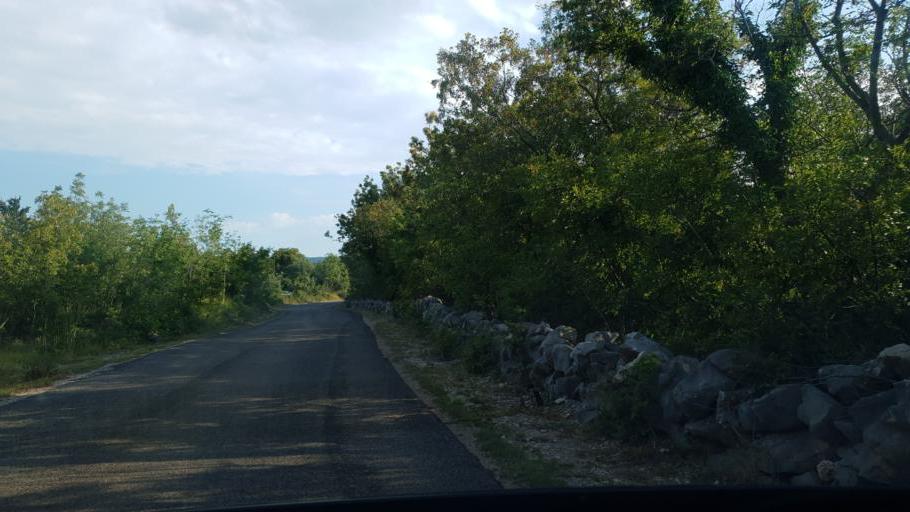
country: HR
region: Primorsko-Goranska
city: Omisalj
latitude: 45.1676
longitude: 14.6059
